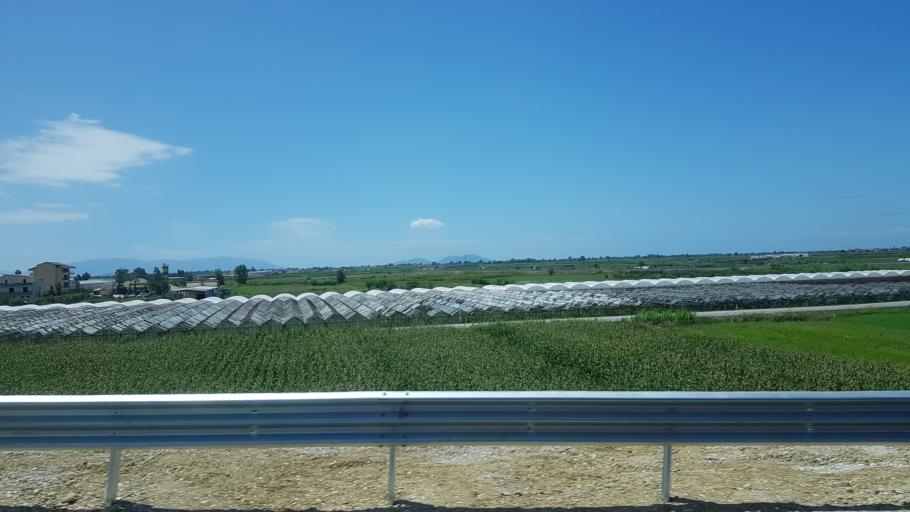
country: AL
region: Fier
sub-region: Rrethi i Fierit
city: Levan
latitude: 40.6706
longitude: 19.4833
